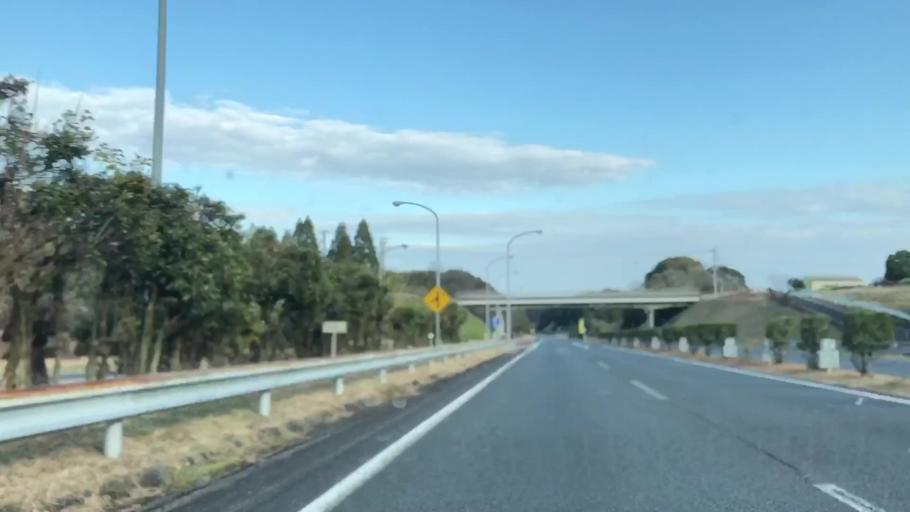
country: JP
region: Miyazaki
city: Miyazaki-shi
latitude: 31.8677
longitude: 131.4020
